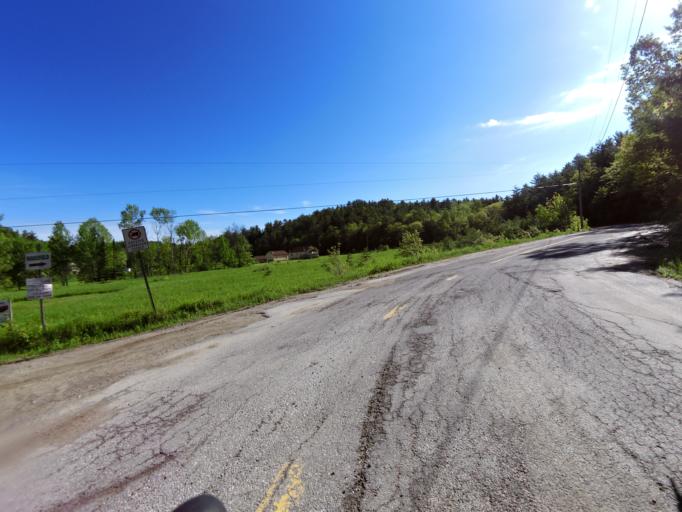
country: CA
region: Quebec
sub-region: Outaouais
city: Wakefield
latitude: 45.6168
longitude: -75.8818
